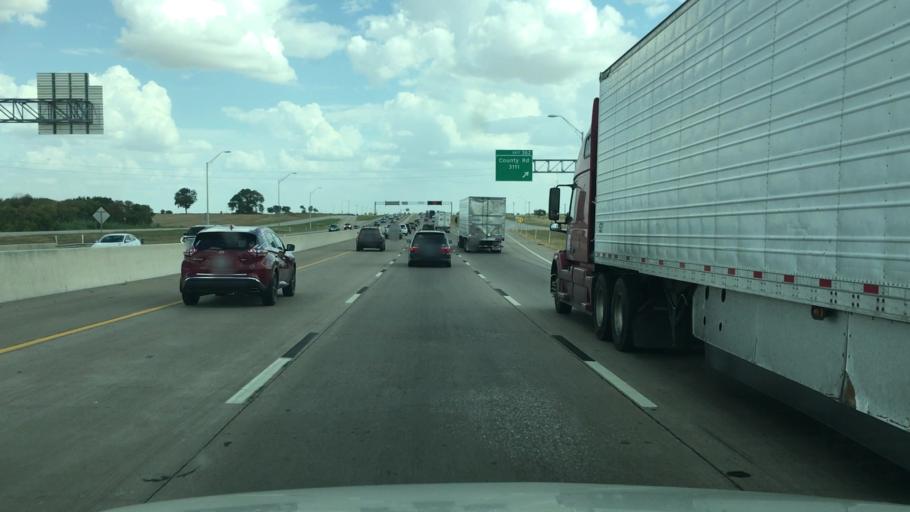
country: US
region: Texas
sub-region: Hill County
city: Hillsboro
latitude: 31.9536
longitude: -97.1139
